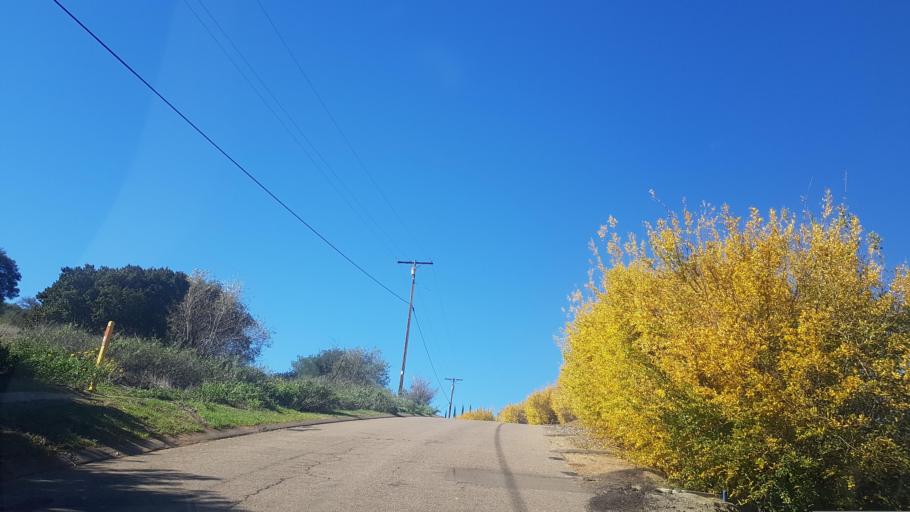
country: US
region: California
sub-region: San Diego County
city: San Pasqual
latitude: 33.0614
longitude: -116.9813
